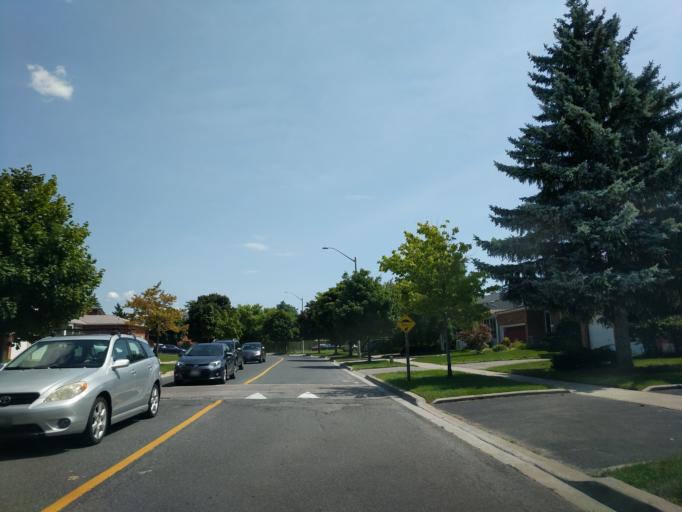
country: CA
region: Ontario
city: Markham
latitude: 43.8233
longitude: -79.3119
